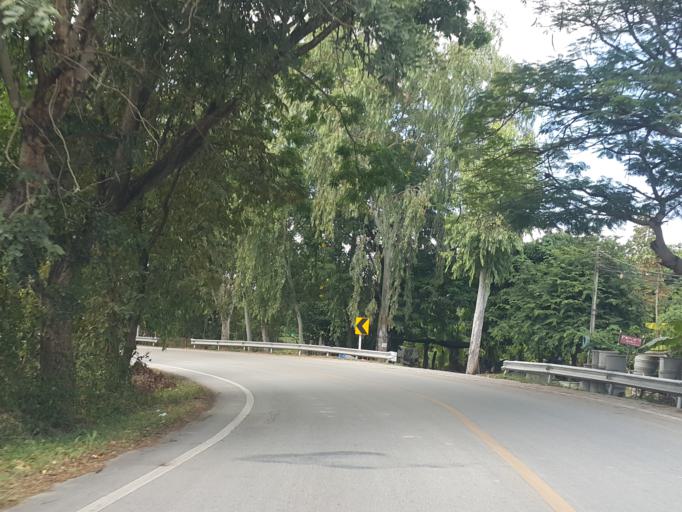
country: TH
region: Lamphun
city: Ban Thi
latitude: 18.6503
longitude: 99.1114
